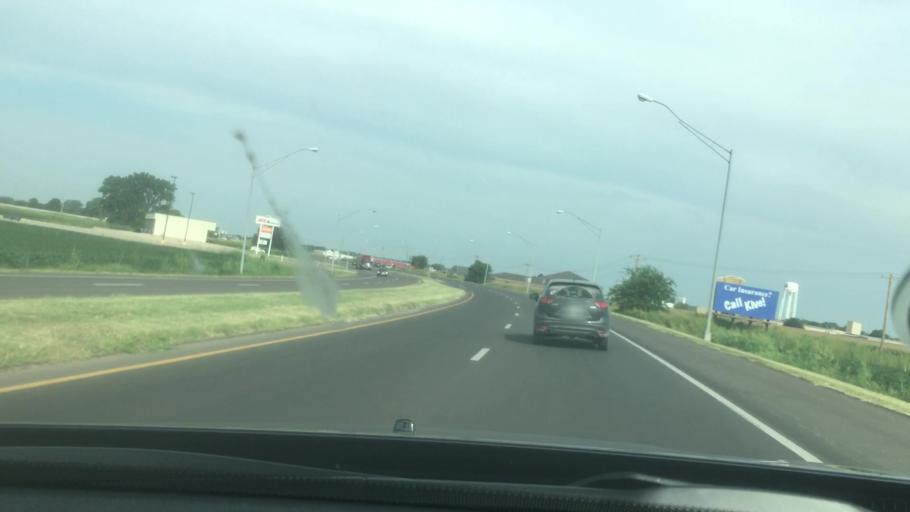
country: US
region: Oklahoma
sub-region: Garvin County
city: Pauls Valley
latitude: 34.7383
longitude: -97.2345
